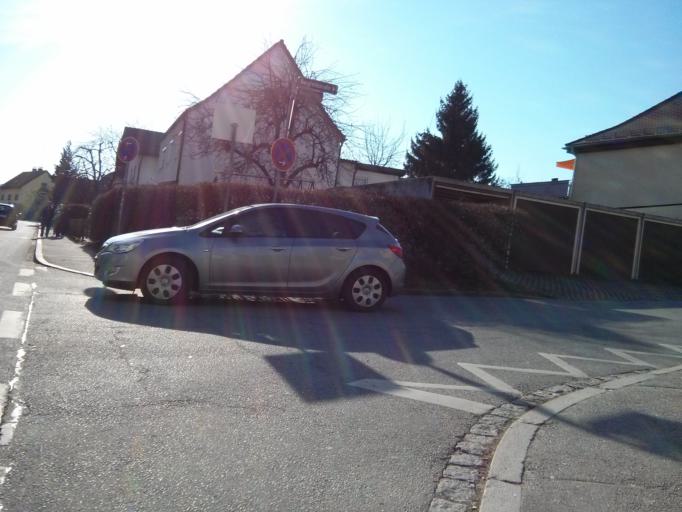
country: DE
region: Bavaria
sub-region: Lower Bavaria
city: Deggendorf
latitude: 48.8431
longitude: 12.9548
